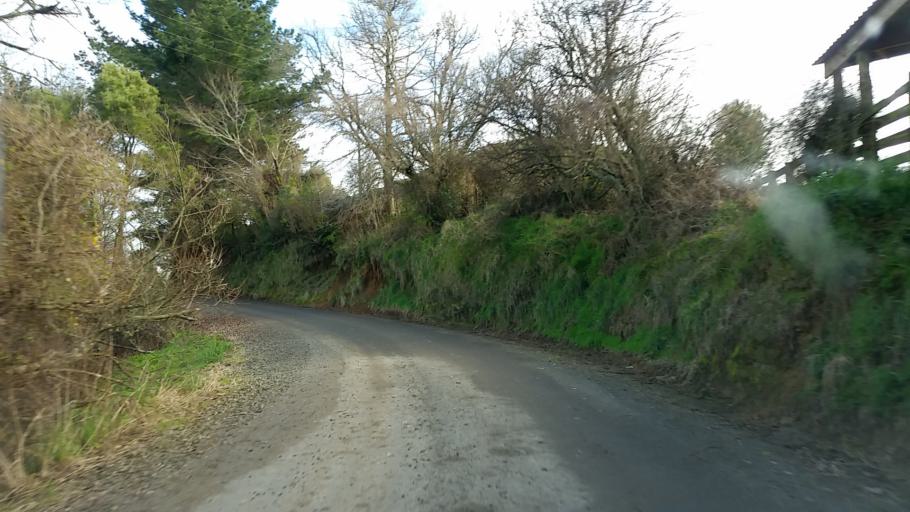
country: NZ
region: Taranaki
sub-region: South Taranaki District
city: Eltham
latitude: -39.2529
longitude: 174.5109
